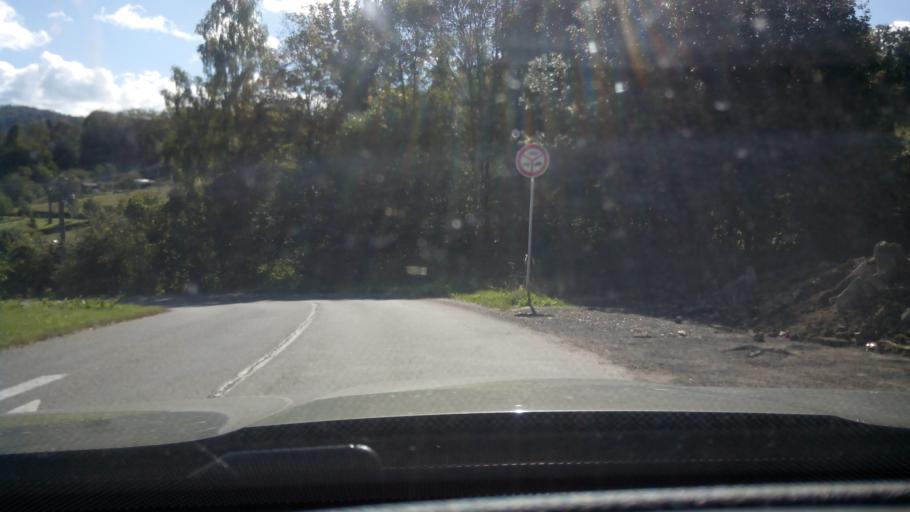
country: CZ
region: Jihocesky
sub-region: Okres Prachatice
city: Vimperk
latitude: 49.0599
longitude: 13.7733
